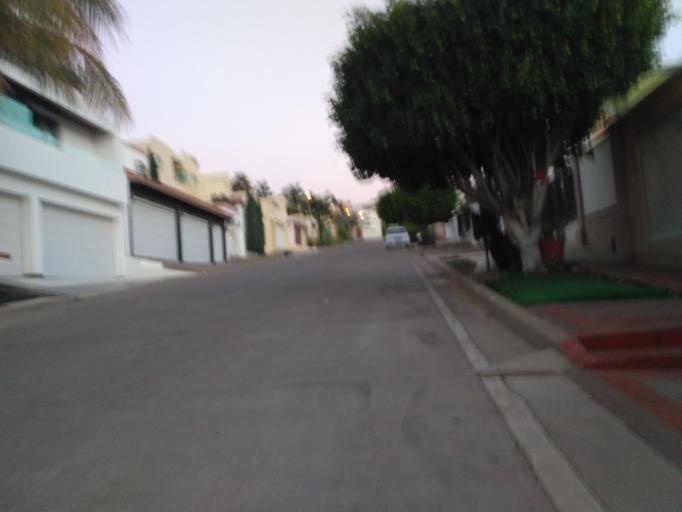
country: MX
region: Sinaloa
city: Culiacan
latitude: 24.7844
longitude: -107.3924
